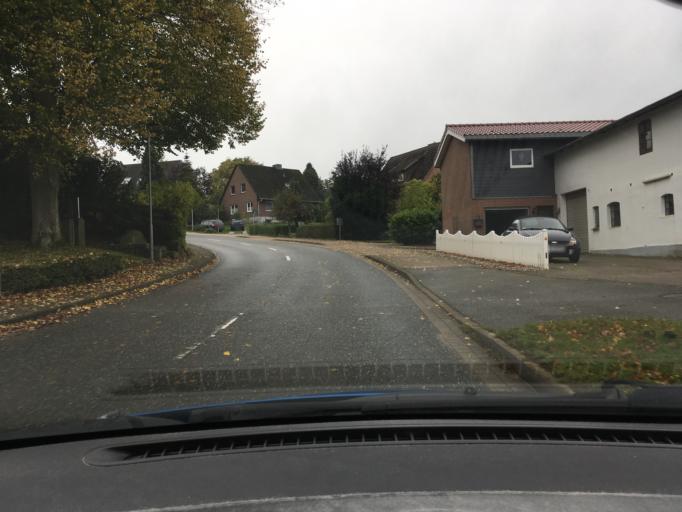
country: DE
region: Schleswig-Holstein
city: Bosdorf
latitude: 54.1262
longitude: 10.4743
